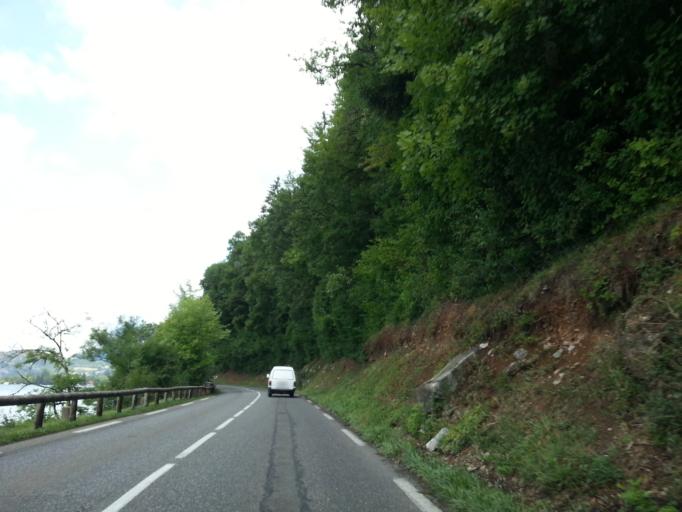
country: FR
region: Rhone-Alpes
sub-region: Departement de la Haute-Savoie
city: Talloires
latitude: 45.8110
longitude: 6.2312
